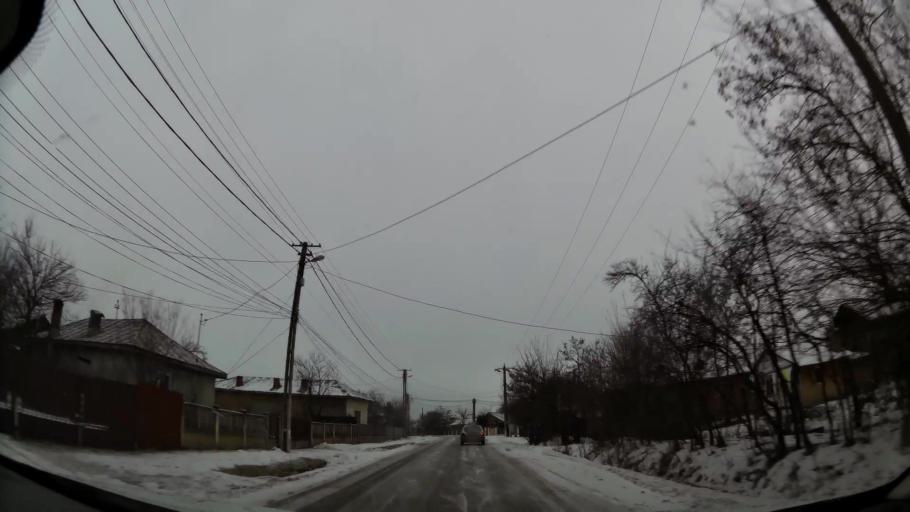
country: RO
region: Prahova
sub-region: Comuna Poenarii-Burchi
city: Ologeni
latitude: 44.7316
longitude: 25.9512
